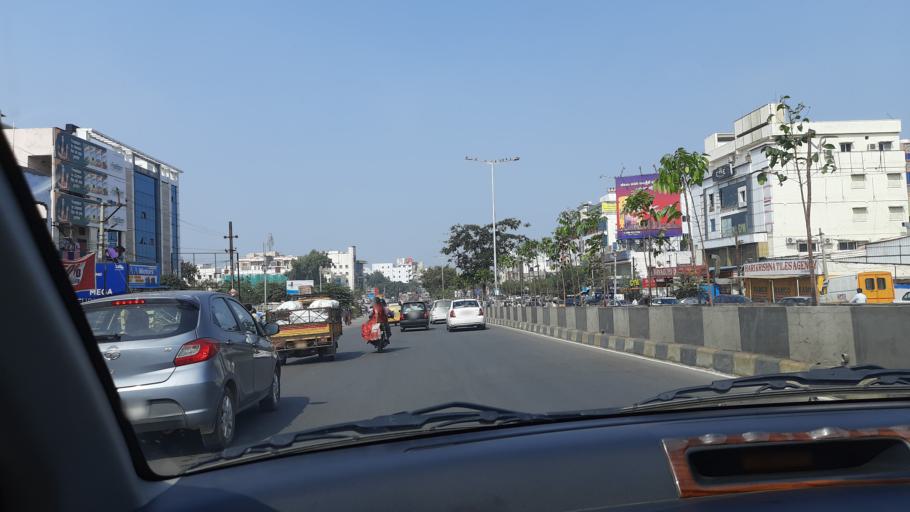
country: IN
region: Telangana
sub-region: Rangareddi
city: Lal Bahadur Nagar
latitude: 17.3618
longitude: 78.5575
